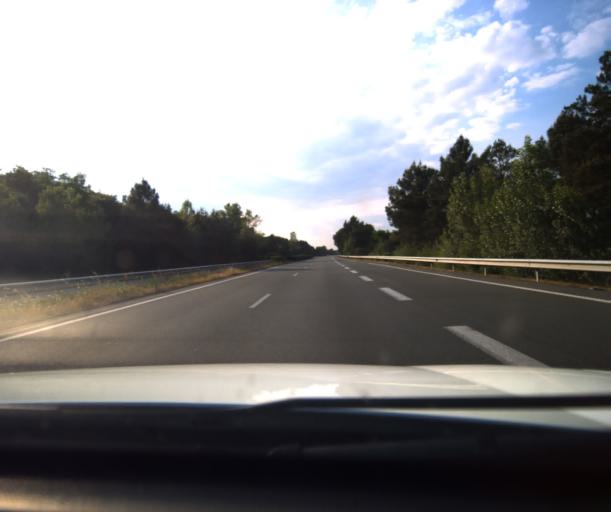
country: FR
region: Midi-Pyrenees
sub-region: Departement du Tarn-et-Garonne
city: Montech
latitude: 43.9660
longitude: 1.2726
